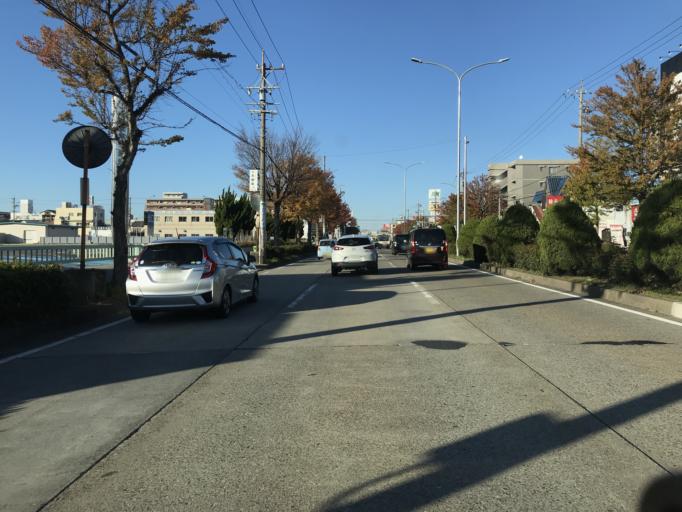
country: JP
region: Aichi
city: Nagoya-shi
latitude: 35.1268
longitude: 136.8690
